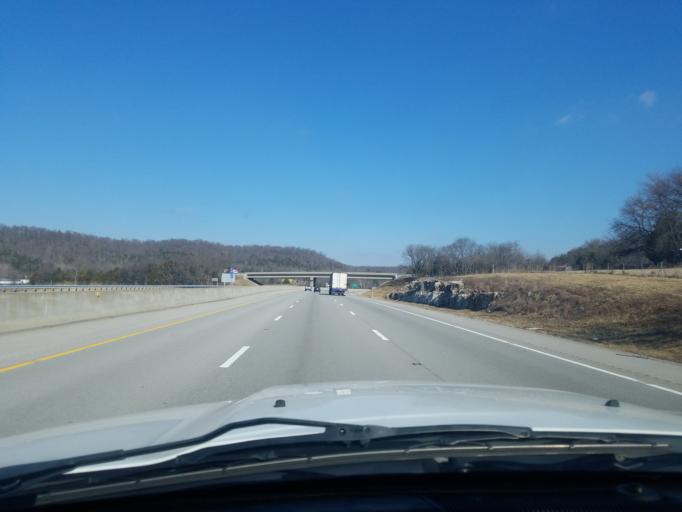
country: US
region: Kentucky
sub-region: Barren County
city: Cave City
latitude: 37.1546
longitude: -85.9708
